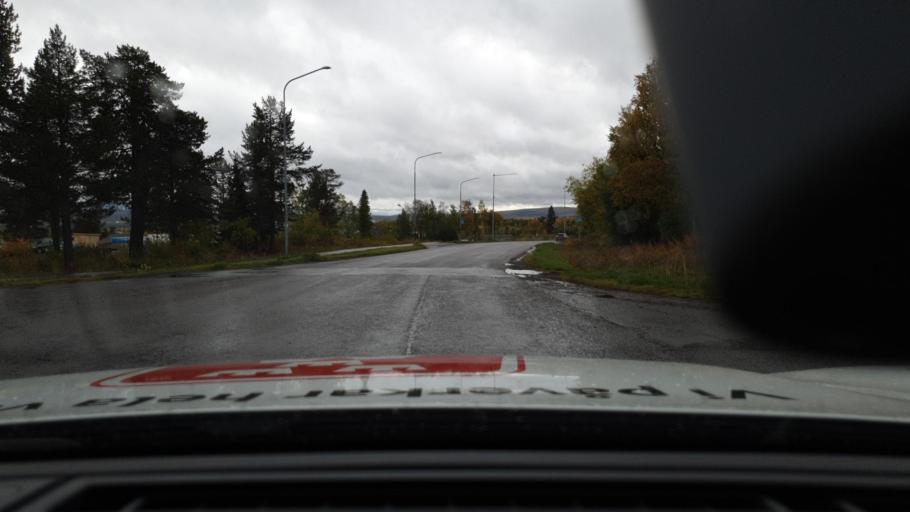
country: SE
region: Norrbotten
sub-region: Kiruna Kommun
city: Kiruna
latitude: 67.8470
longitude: 20.2873
